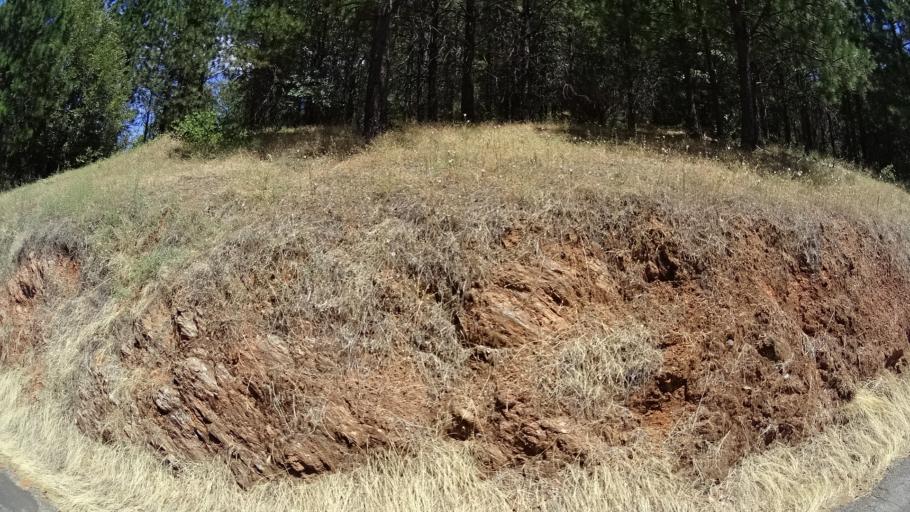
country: US
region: California
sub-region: Calaveras County
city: Forest Meadows
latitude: 38.1980
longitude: -120.4450
